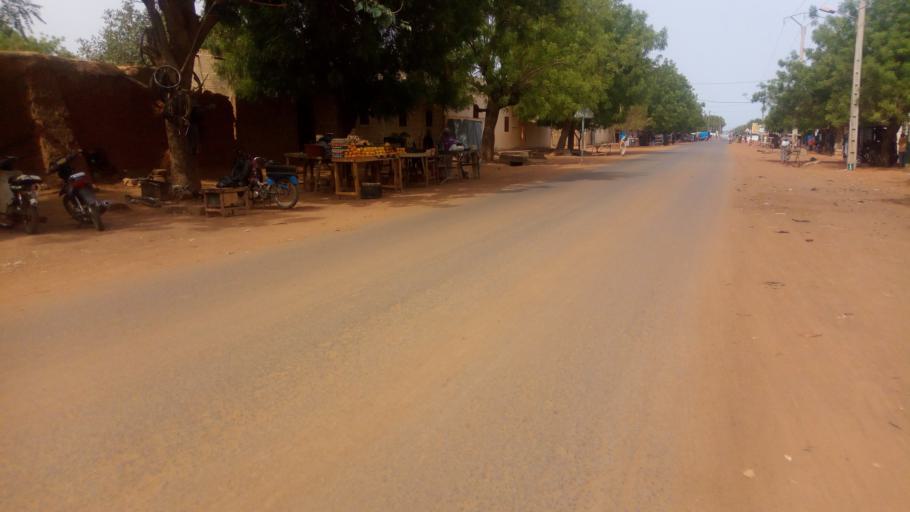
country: ML
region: Segou
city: Segou
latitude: 13.4345
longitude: -6.2917
